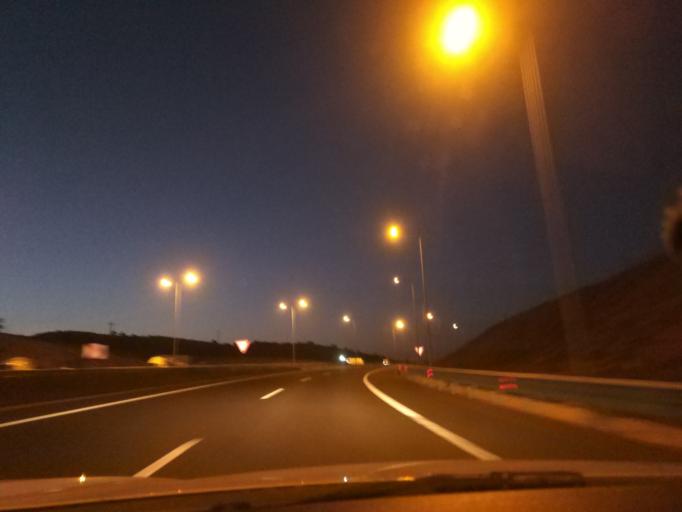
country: TR
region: Istanbul
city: Sancaktepe
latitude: 41.0488
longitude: 29.2763
